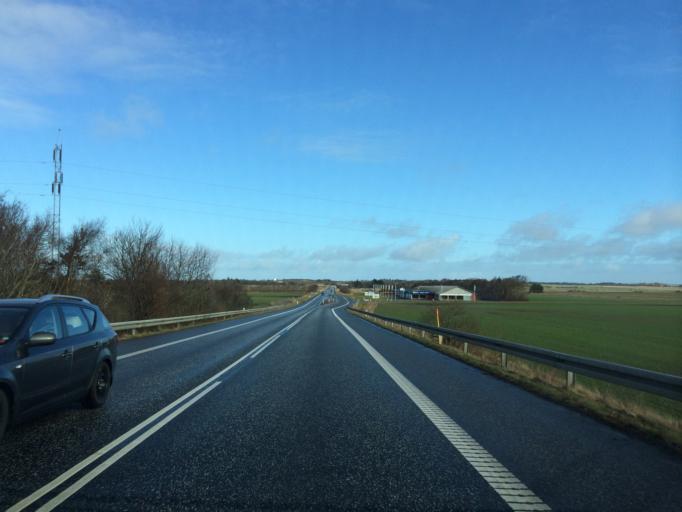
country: DK
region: Central Jutland
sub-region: Holstebro Kommune
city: Ulfborg
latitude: 56.2808
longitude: 8.3284
